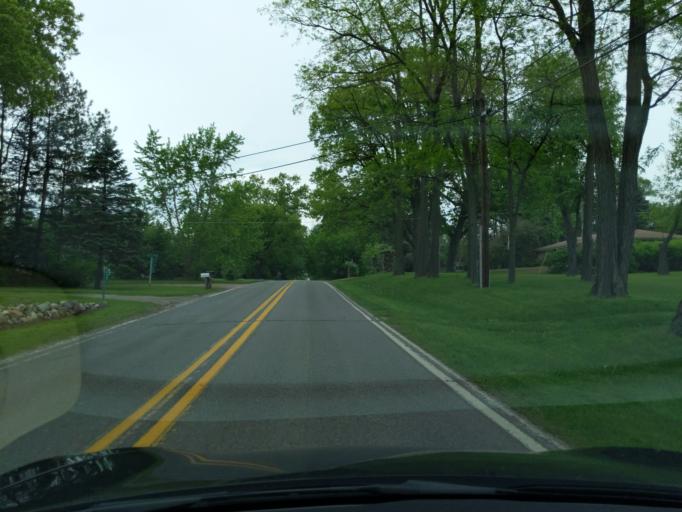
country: US
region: Michigan
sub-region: Ingham County
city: Leslie
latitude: 42.3614
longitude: -84.3489
